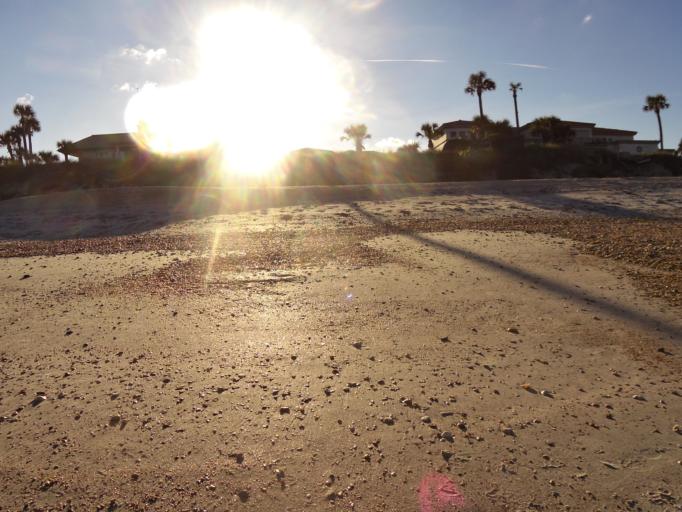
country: US
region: Florida
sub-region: Saint Johns County
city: Sawgrass
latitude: 30.1843
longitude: -81.3615
